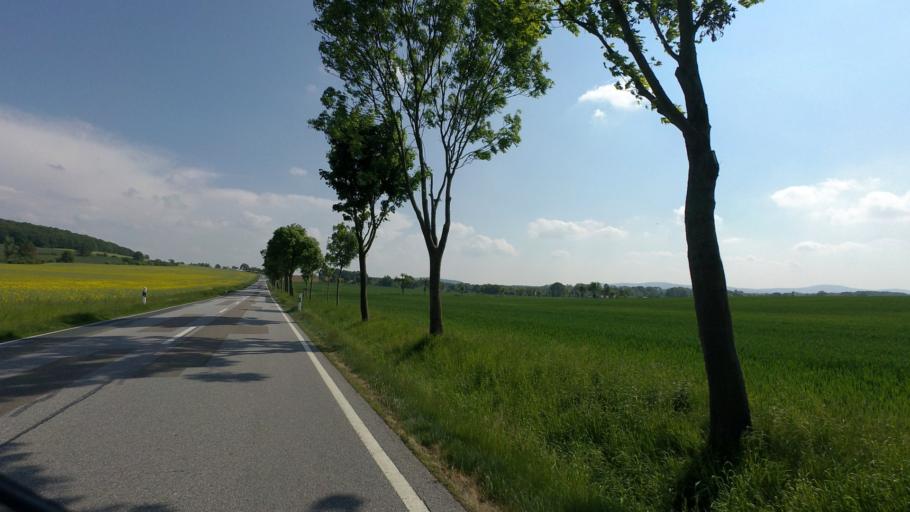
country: DE
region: Saxony
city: Weissenberg
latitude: 51.1849
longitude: 14.6431
